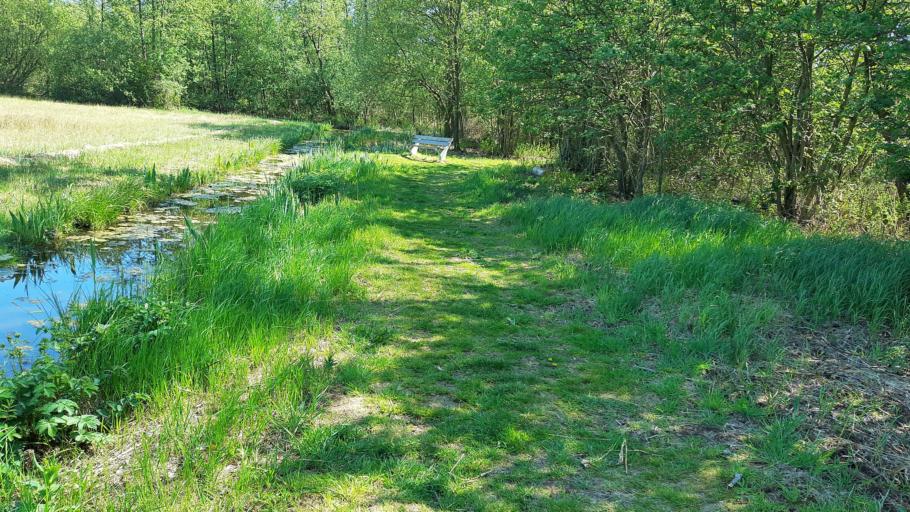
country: NL
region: South Holland
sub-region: Gemeente Gouda
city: Gouda
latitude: 51.9771
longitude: 4.6840
